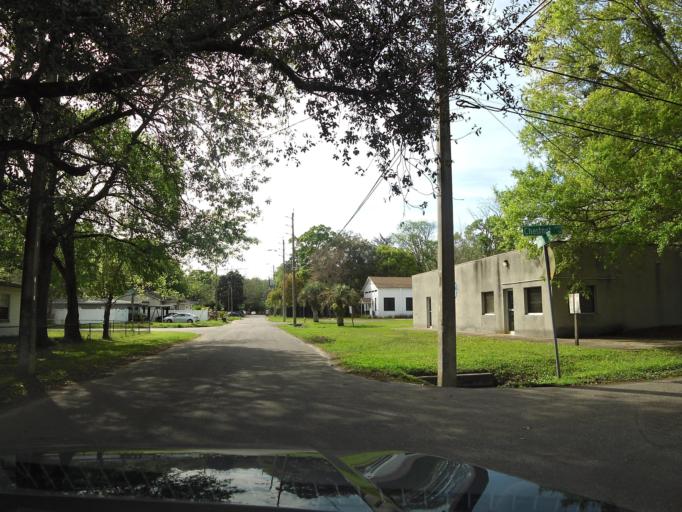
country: US
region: Florida
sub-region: Duval County
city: Jacksonville
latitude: 30.3183
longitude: -81.7172
